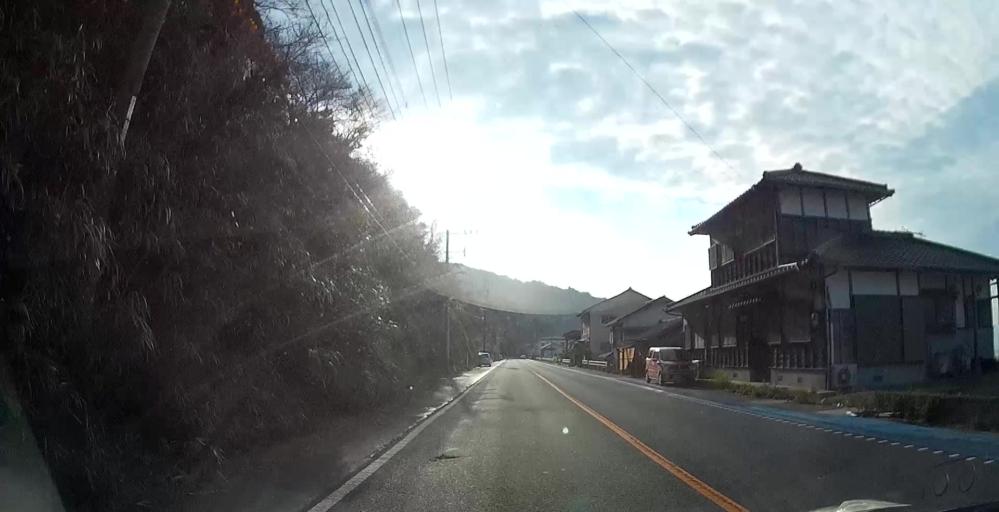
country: JP
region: Kumamoto
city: Matsubase
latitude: 32.6568
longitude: 130.5129
